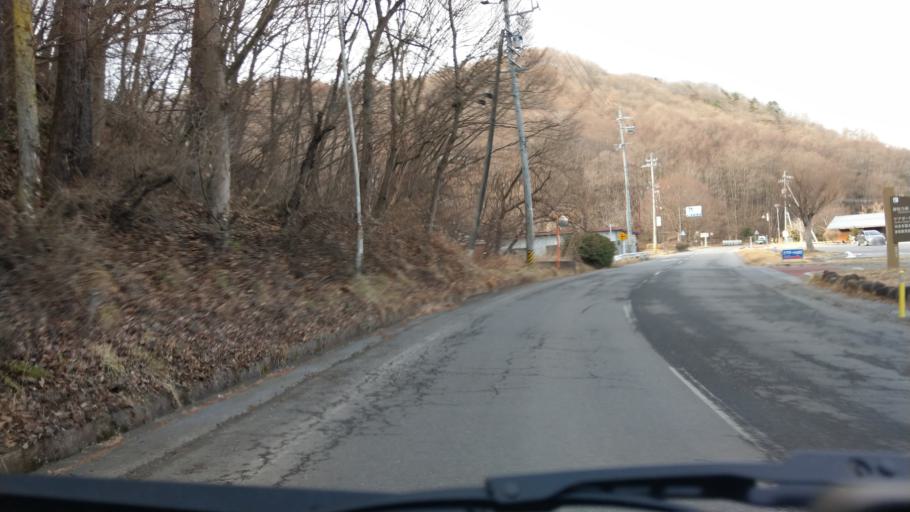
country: JP
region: Nagano
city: Komoro
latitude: 36.3343
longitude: 138.3606
